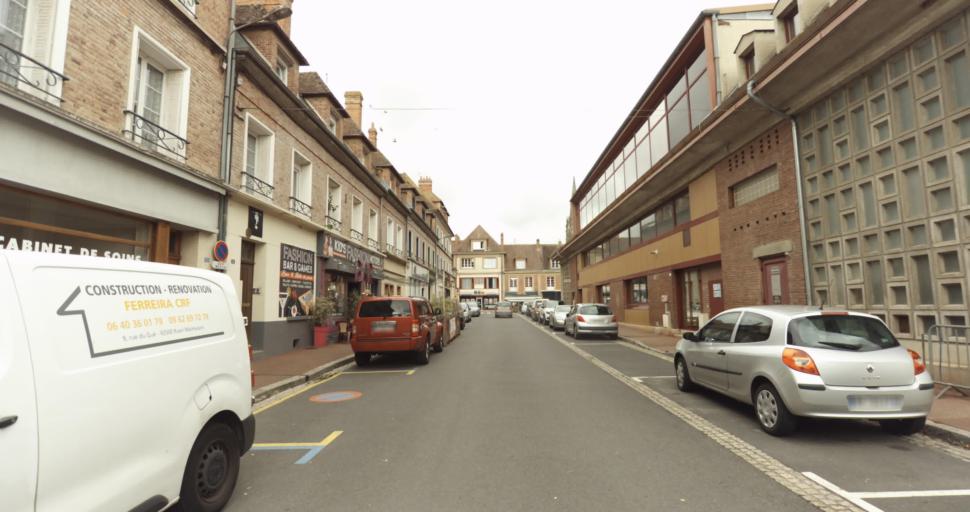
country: FR
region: Lower Normandy
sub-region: Departement de l'Orne
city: Vimoutiers
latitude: 48.9275
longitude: 0.1976
